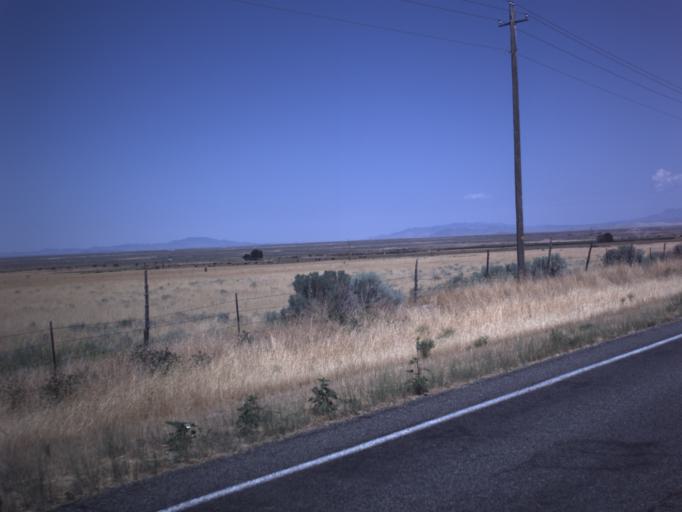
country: US
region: Utah
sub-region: Millard County
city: Delta
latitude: 39.3921
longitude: -112.3355
